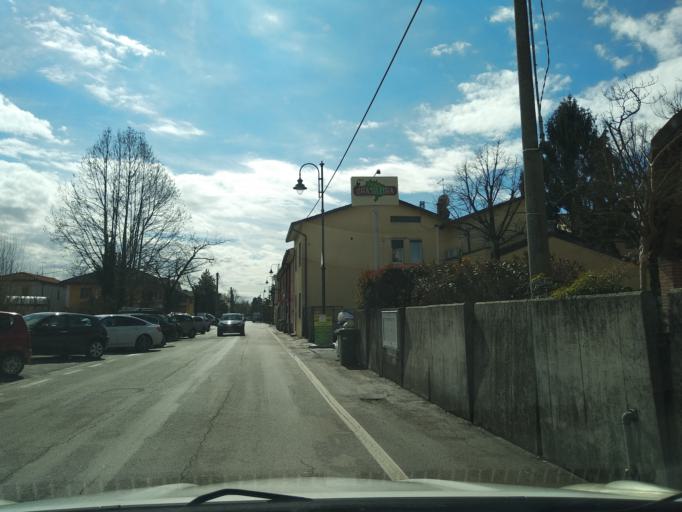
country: IT
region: Veneto
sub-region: Provincia di Vicenza
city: Bolzano Vicentino
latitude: 45.6018
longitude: 11.6141
